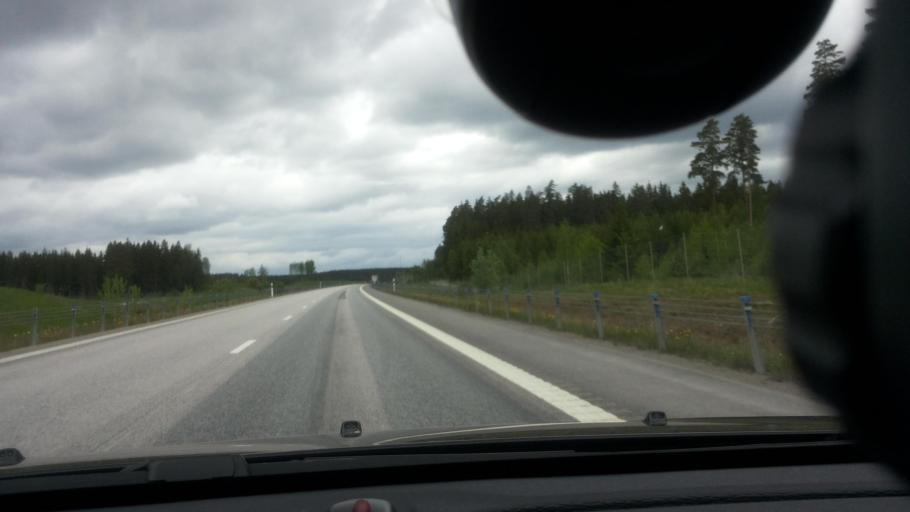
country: SE
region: Uppsala
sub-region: Osthammars Kommun
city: Bjorklinge
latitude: 60.0892
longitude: 17.5833
